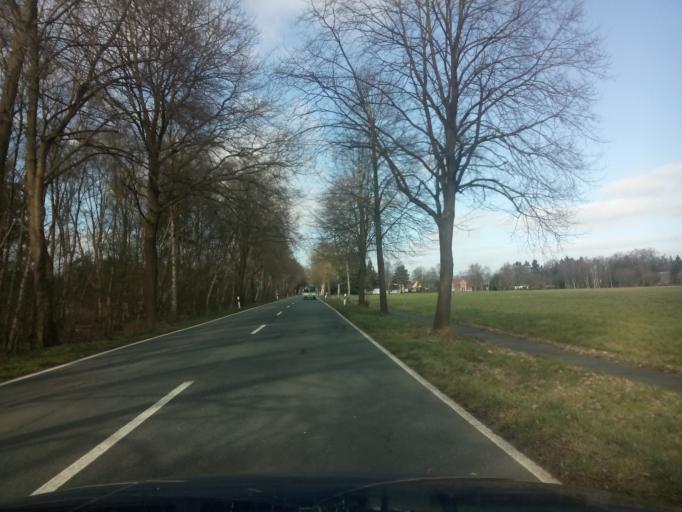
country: DE
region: Lower Saxony
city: Grasberg
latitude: 53.2074
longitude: 8.9653
